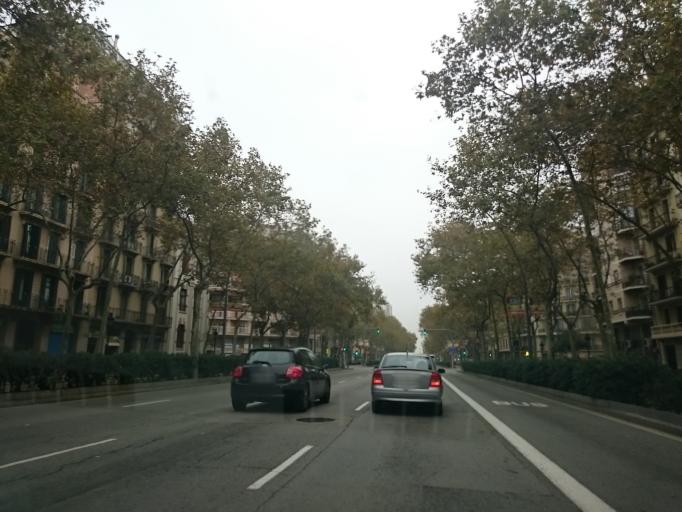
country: ES
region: Catalonia
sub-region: Provincia de Barcelona
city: Ciutat Vella
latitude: 41.3969
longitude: 2.1783
